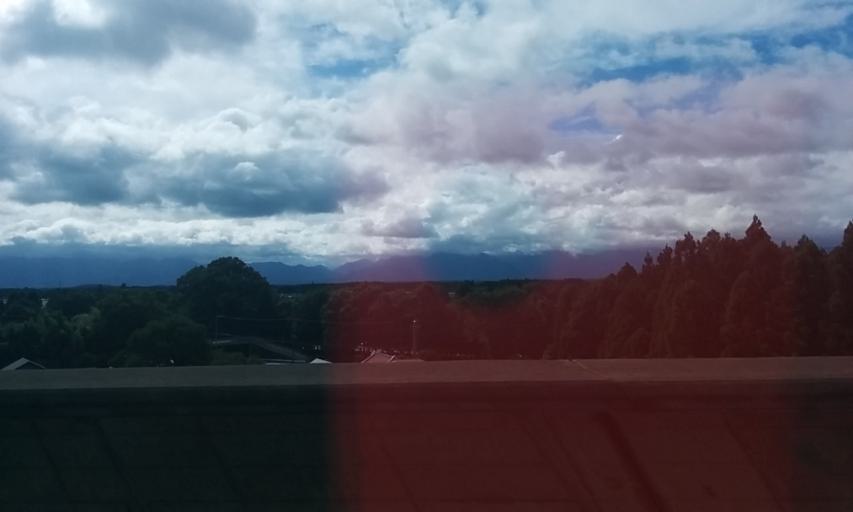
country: JP
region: Tochigi
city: Kuroiso
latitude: 36.9226
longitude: 140.0138
